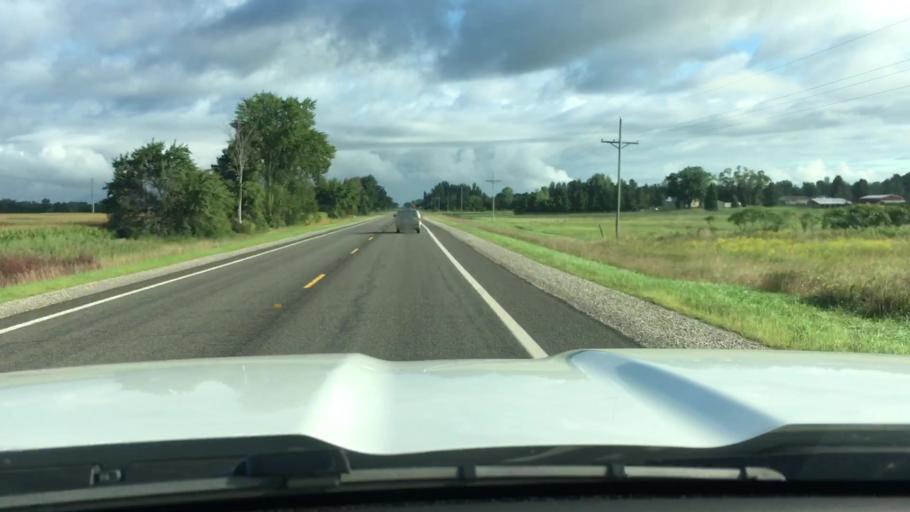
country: US
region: Michigan
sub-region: Tuscola County
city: Caro
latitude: 43.3903
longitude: -83.3834
